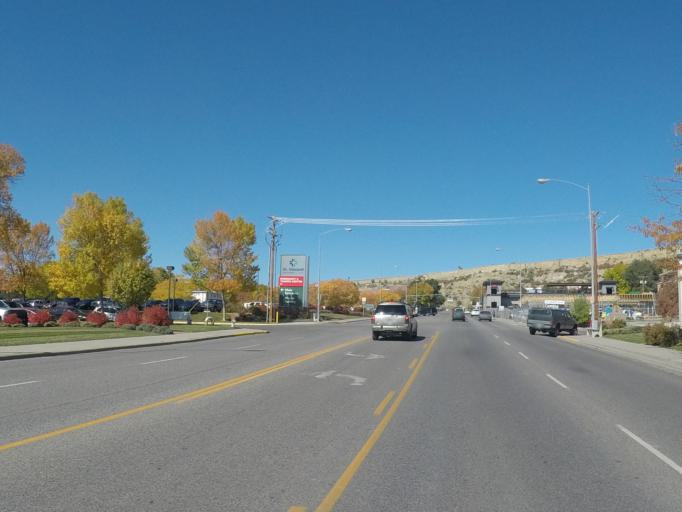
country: US
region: Montana
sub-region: Yellowstone County
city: Billings
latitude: 45.7938
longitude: -108.5155
